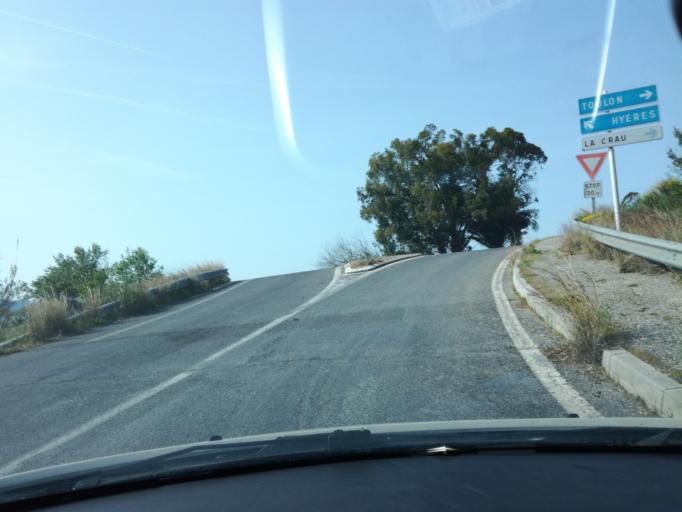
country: FR
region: Provence-Alpes-Cote d'Azur
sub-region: Departement du Var
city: La Crau
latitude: 43.1244
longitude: 6.0902
